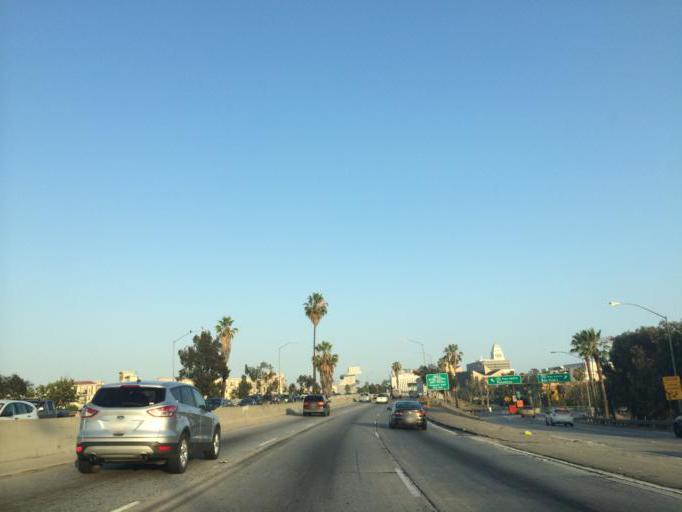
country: US
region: California
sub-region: Los Angeles County
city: Los Angeles
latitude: 34.0641
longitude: -118.2504
